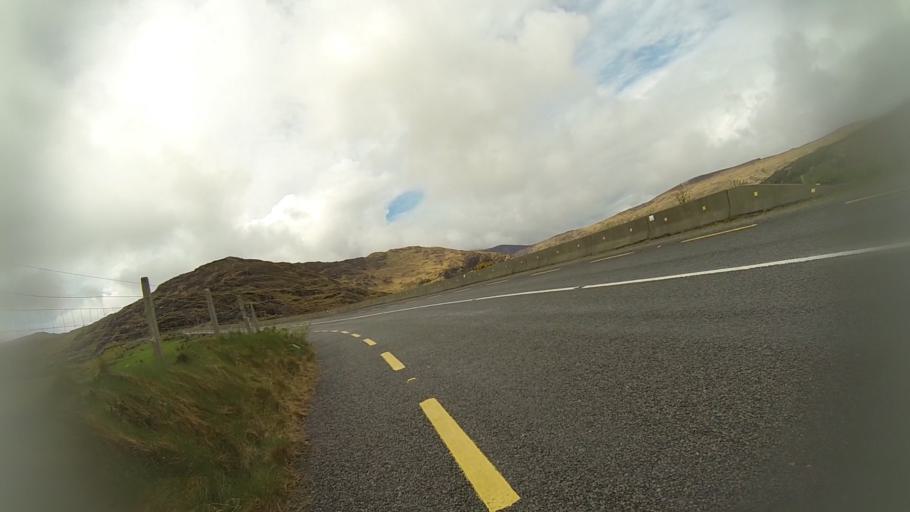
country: IE
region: Munster
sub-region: Ciarrai
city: Kenmare
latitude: 51.7950
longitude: -9.5891
